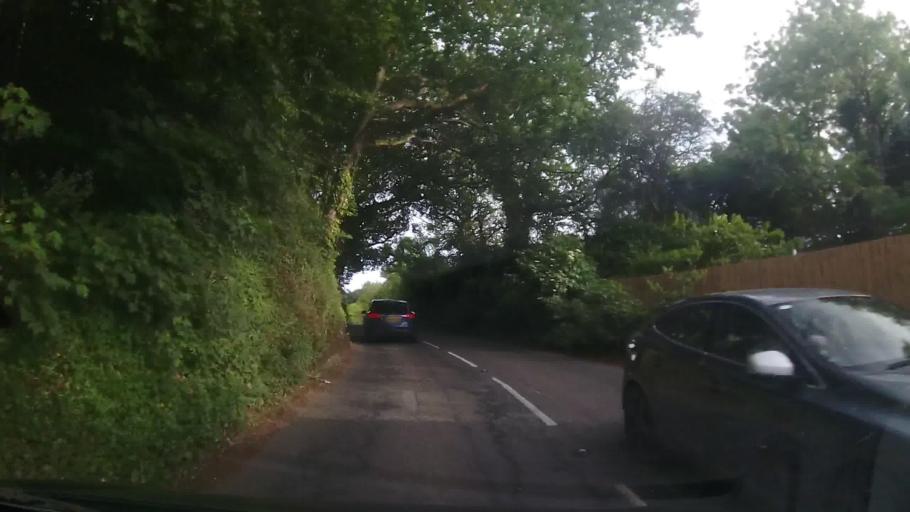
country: GB
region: England
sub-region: Devon
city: Kingsbridge
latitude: 50.2742
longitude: -3.7611
